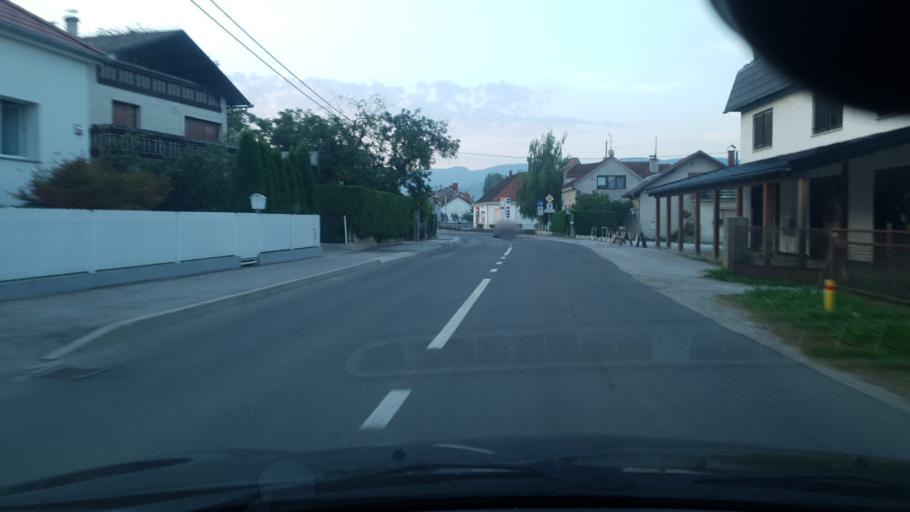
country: HR
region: Krapinsko-Zagorska
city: Marija Bistrica
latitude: 46.0070
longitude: 16.1124
